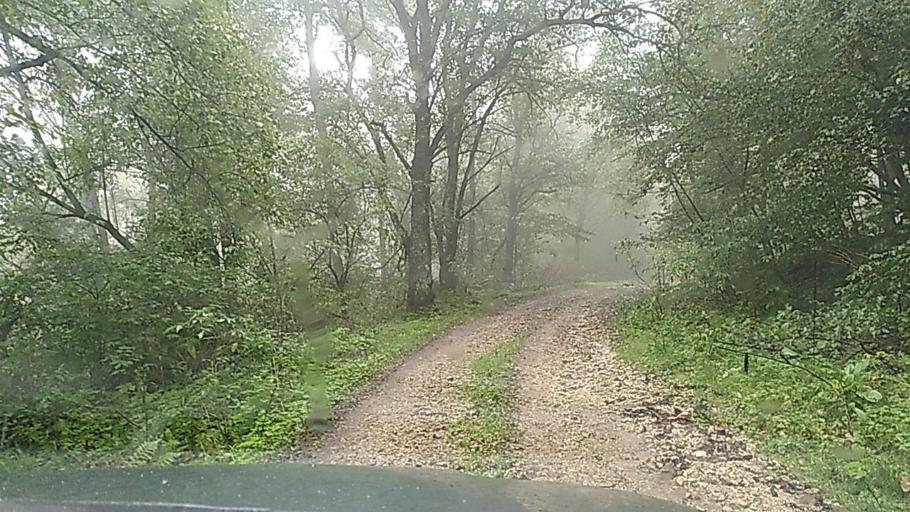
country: RU
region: Kabardino-Balkariya
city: Belaya Rechka
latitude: 43.3613
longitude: 43.4130
